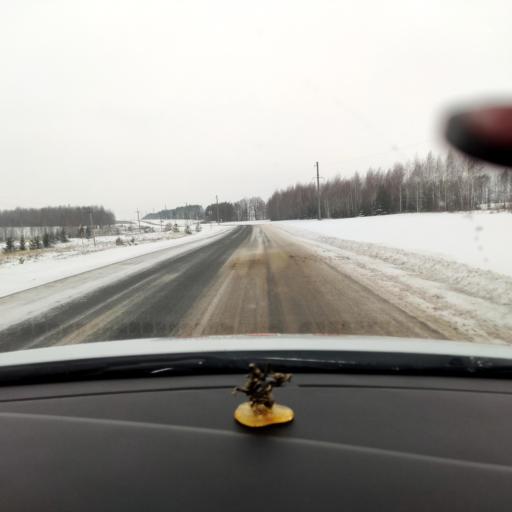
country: RU
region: Tatarstan
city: Vysokaya Gora
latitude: 56.1129
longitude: 49.1581
